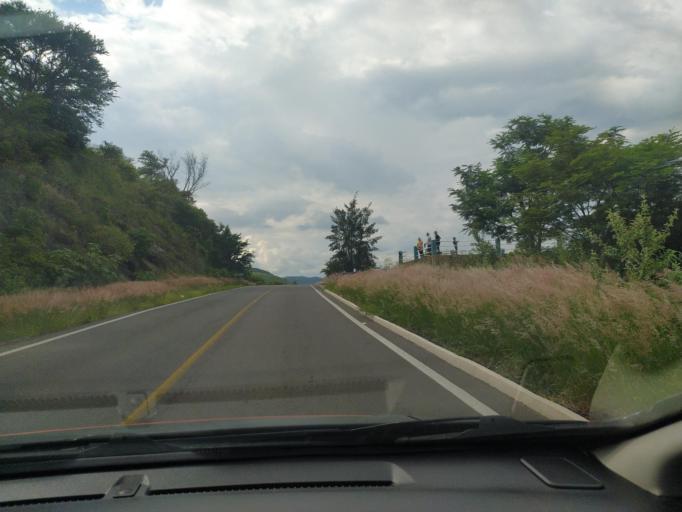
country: MX
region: Jalisco
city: Villa Corona
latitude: 20.3956
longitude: -103.6786
